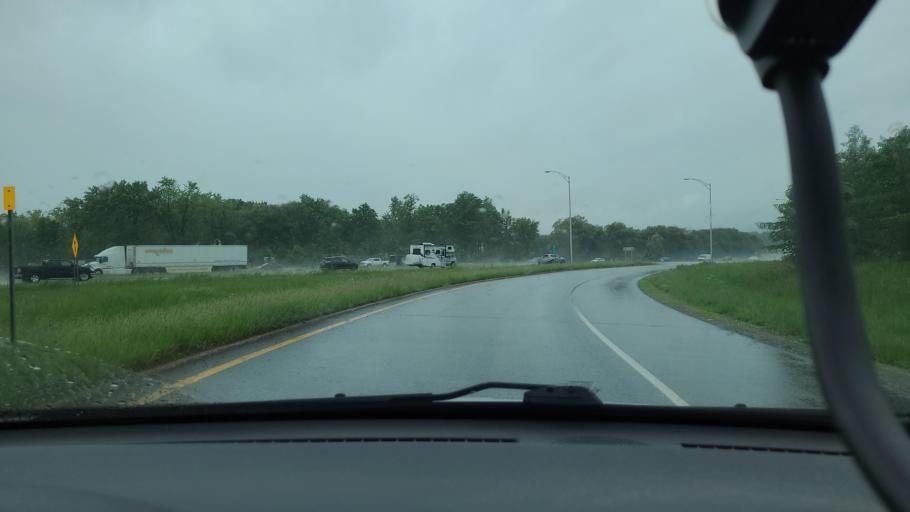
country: CA
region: Quebec
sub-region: Monteregie
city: Beloeil
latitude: 45.6068
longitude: -73.1047
